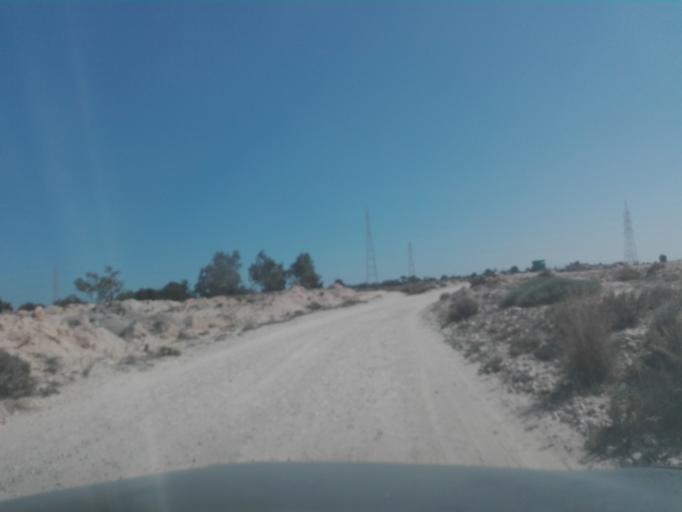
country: TN
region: Qabis
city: Gabes
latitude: 33.8747
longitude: 10.0282
